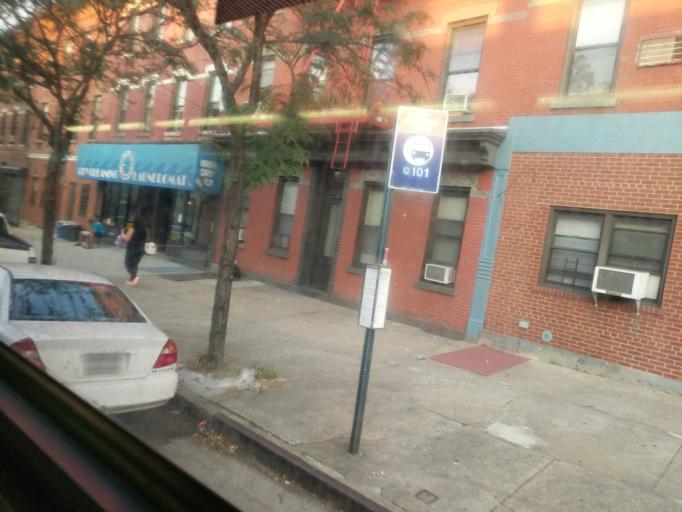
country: US
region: New York
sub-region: Queens County
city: Long Island City
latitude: 40.7748
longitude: -73.9036
